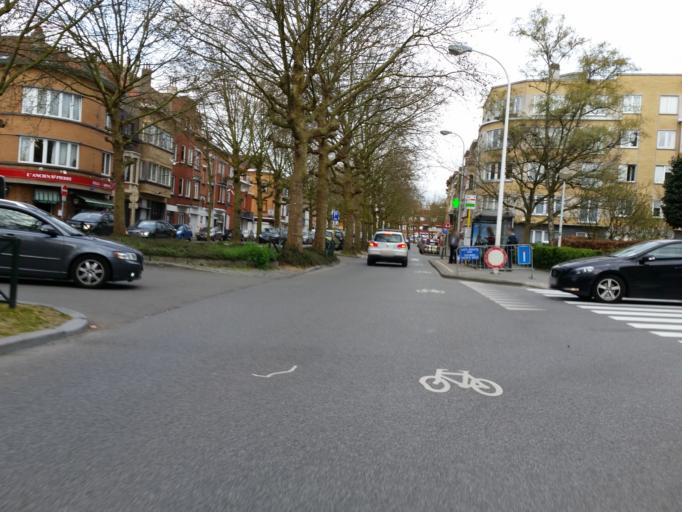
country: BE
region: Flanders
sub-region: Provincie Vlaams-Brabant
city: Wemmel
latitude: 50.8753
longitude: 4.3201
